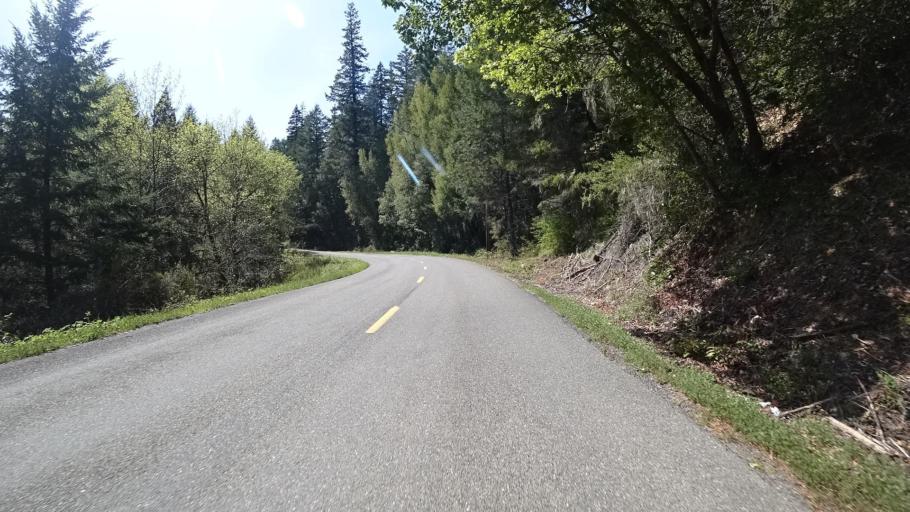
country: US
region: California
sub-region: Humboldt County
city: Redway
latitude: 40.3348
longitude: -123.6829
